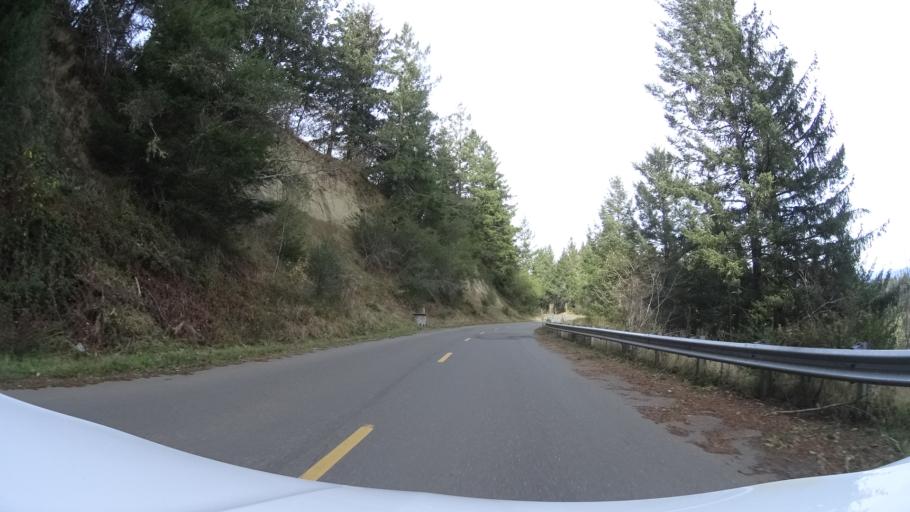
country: US
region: California
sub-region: Humboldt County
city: Ferndale
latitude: 40.5506
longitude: -124.2742
